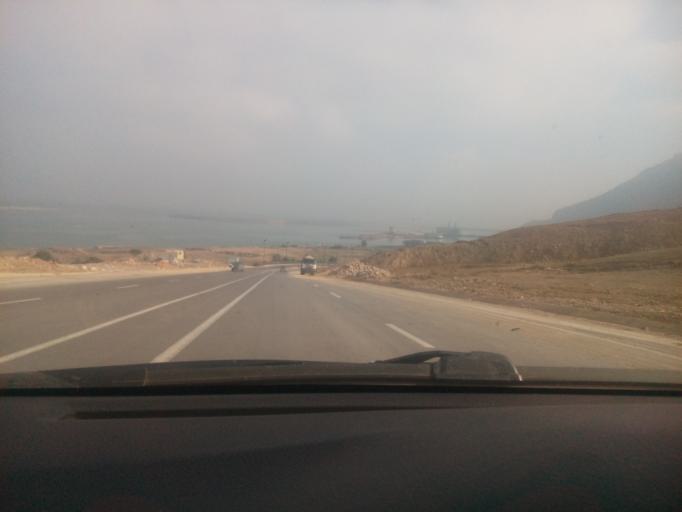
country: DZ
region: Oran
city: Mers el Kebir
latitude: 35.7140
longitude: -0.6942
